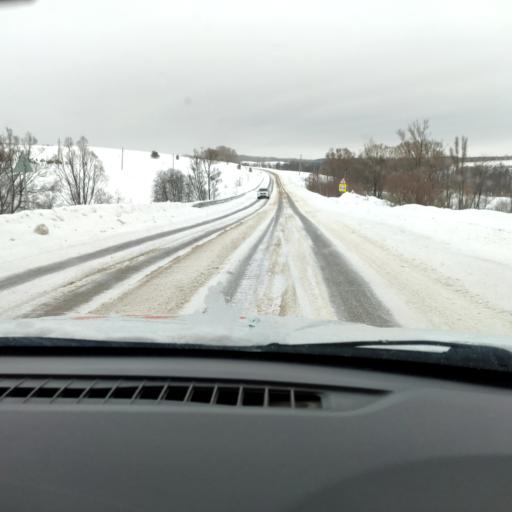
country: RU
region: Bashkortostan
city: Blagoveshchensk
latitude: 55.0514
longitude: 56.0152
